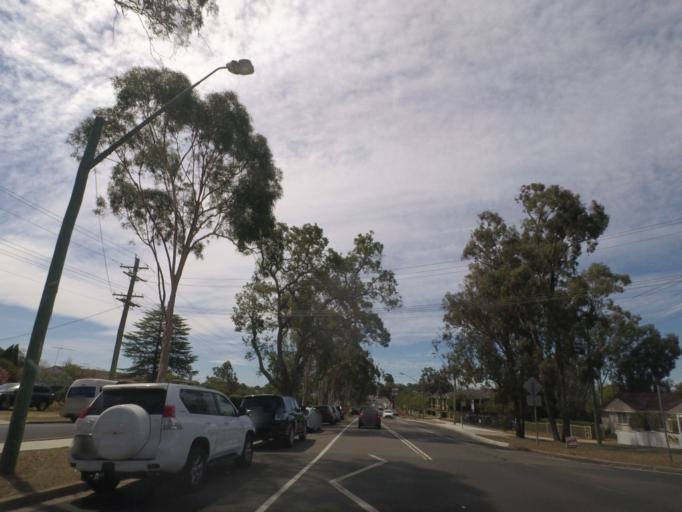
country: AU
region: New South Wales
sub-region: Camden
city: Camden South
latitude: -34.0714
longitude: 150.6945
